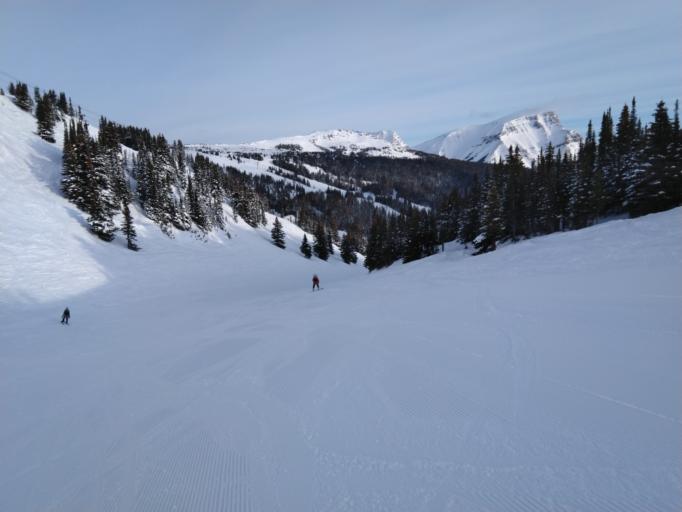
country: CA
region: Alberta
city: Banff
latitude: 51.0730
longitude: -115.7834
